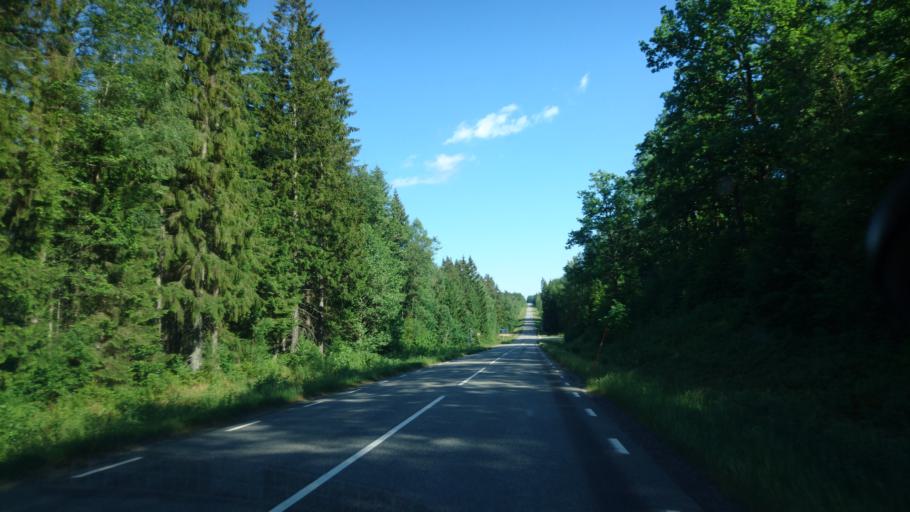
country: SE
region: Skane
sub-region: Osby Kommun
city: Lonsboda
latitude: 56.4435
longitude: 14.2404
